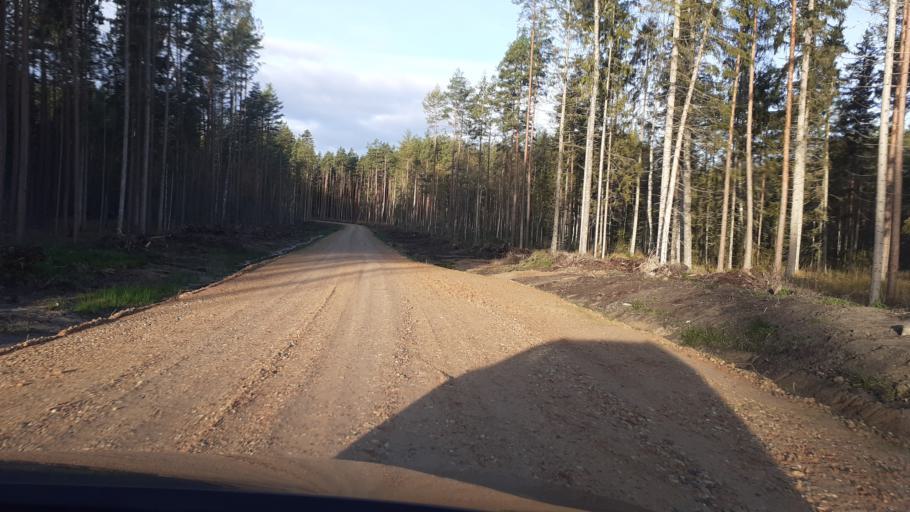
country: LV
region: Kuldigas Rajons
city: Kuldiga
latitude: 56.8499
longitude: 22.0899
